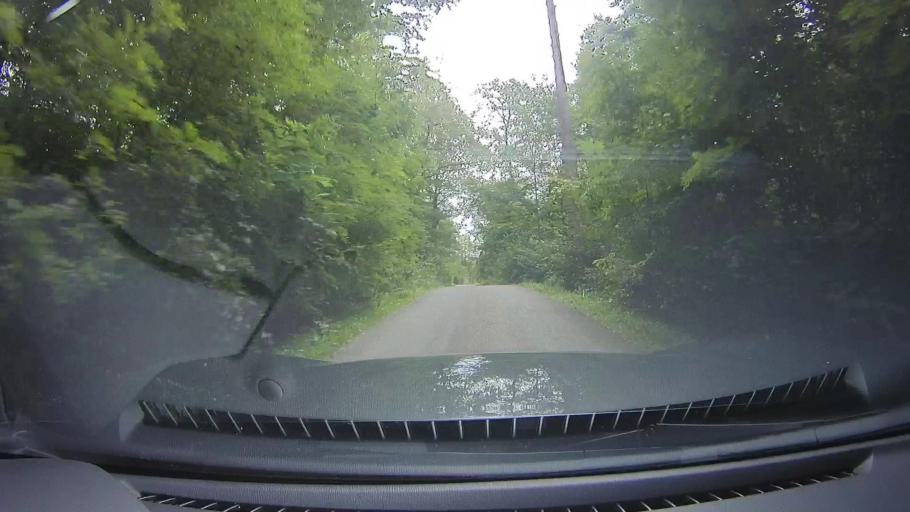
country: DE
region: Baden-Wuerttemberg
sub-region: Regierungsbezirk Stuttgart
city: Sulzbach an der Murr
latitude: 48.9789
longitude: 9.5061
